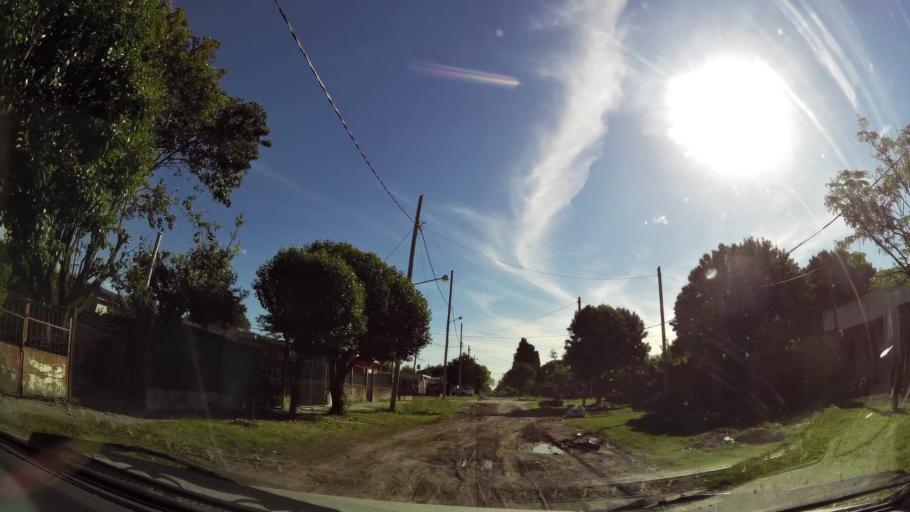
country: AR
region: Buenos Aires
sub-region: Partido de Almirante Brown
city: Adrogue
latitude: -34.8276
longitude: -58.3496
